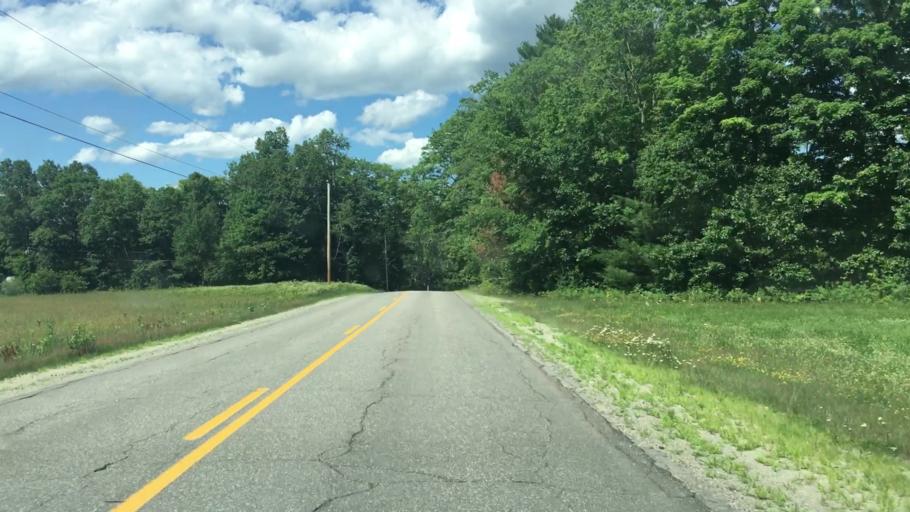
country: US
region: Maine
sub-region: Franklin County
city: Chesterville
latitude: 44.5852
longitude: -70.0889
